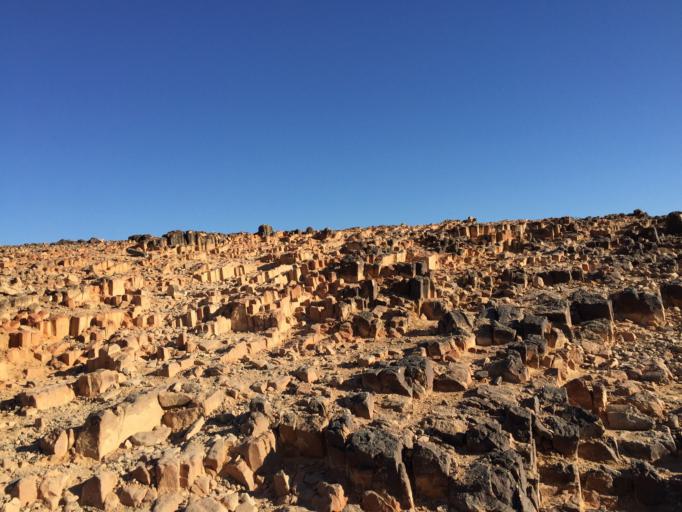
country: IL
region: Southern District
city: Mitzpe Ramon
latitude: 30.6154
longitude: 34.8386
